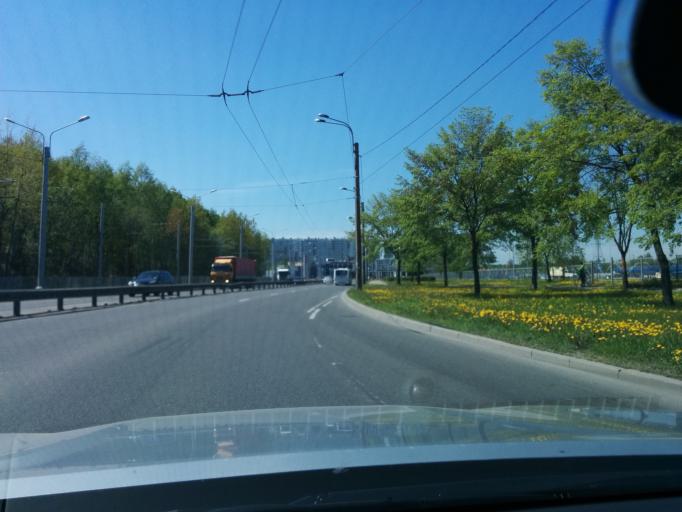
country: RU
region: St.-Petersburg
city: Krasnogvargeisky
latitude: 59.9396
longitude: 30.4572
